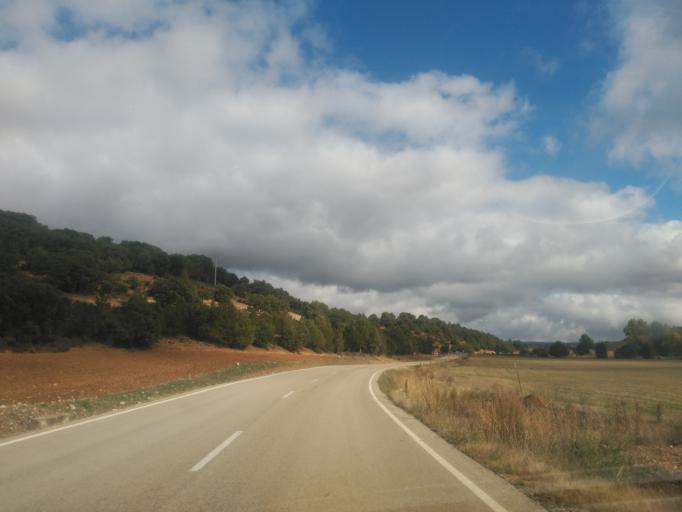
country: ES
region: Castille and Leon
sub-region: Provincia de Soria
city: Alcubilla de Avellaneda
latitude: 41.7403
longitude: -3.2929
